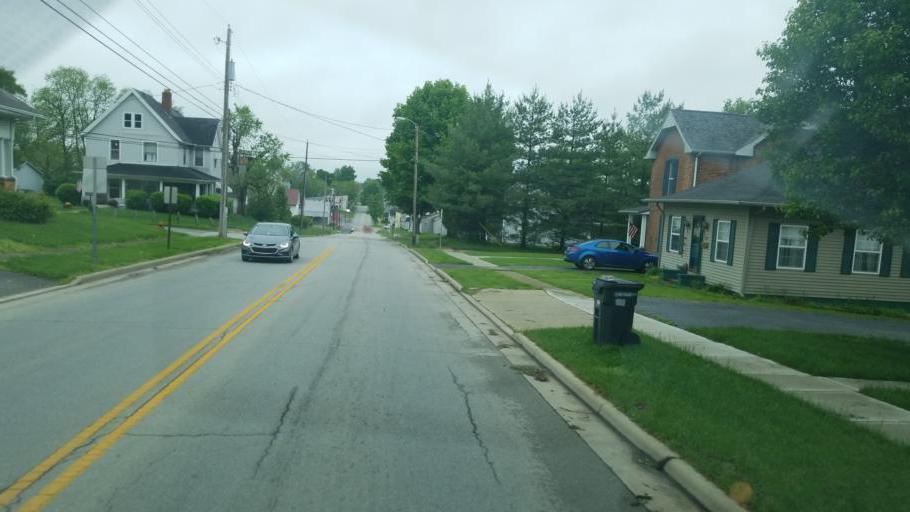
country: US
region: Ohio
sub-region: Highland County
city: Hillsboro
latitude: 39.2094
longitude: -83.6123
